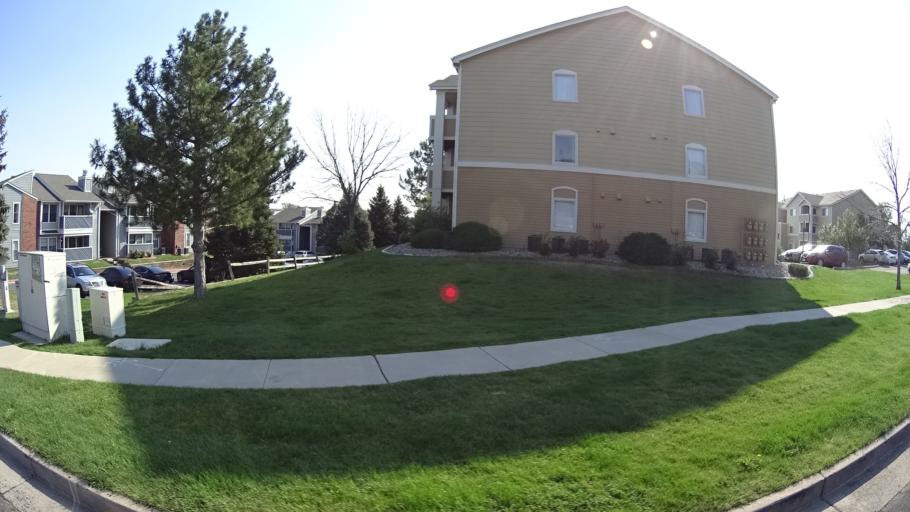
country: US
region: Colorado
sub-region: El Paso County
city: Stratmoor
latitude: 38.7722
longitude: -104.8107
